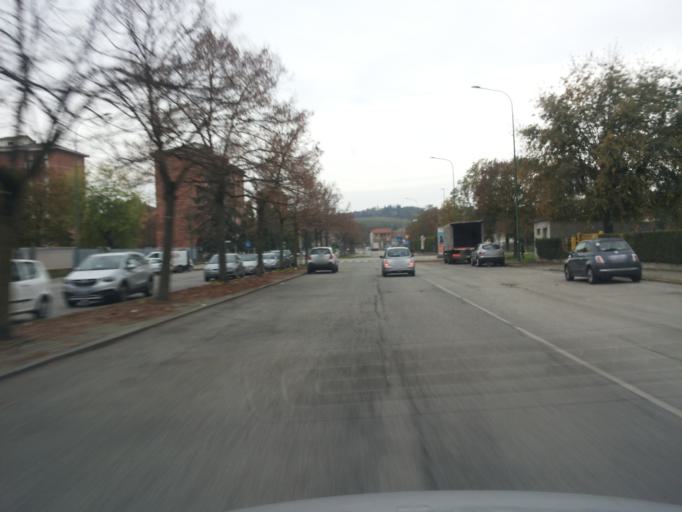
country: IT
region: Piedmont
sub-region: Provincia di Alessandria
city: Casale Monferrato
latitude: 45.1239
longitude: 8.4557
